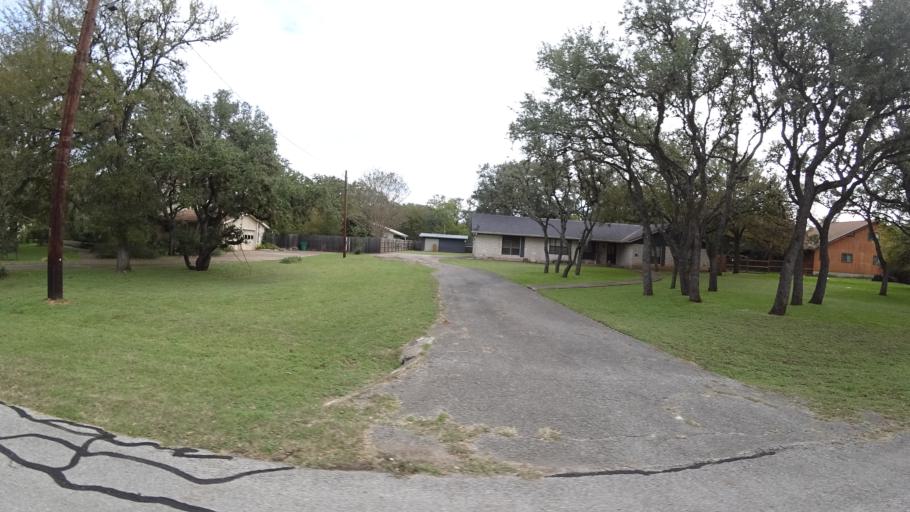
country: US
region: Texas
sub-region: Travis County
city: Shady Hollow
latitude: 30.1366
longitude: -97.8916
